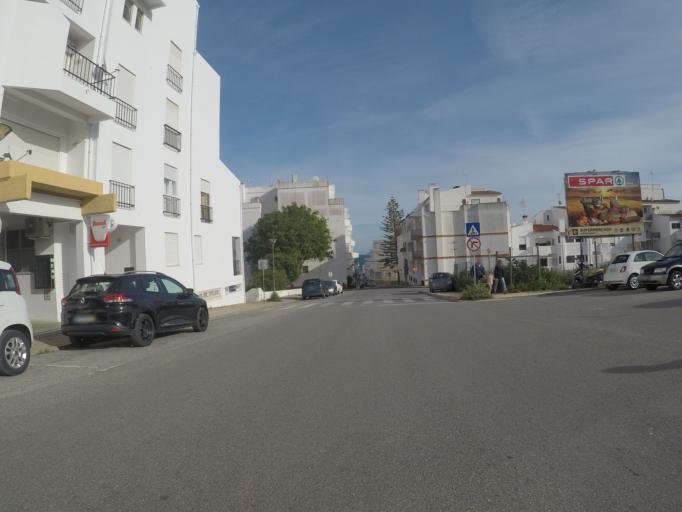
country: PT
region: Faro
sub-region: Lagos
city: Lagos
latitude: 37.0870
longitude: -8.7312
